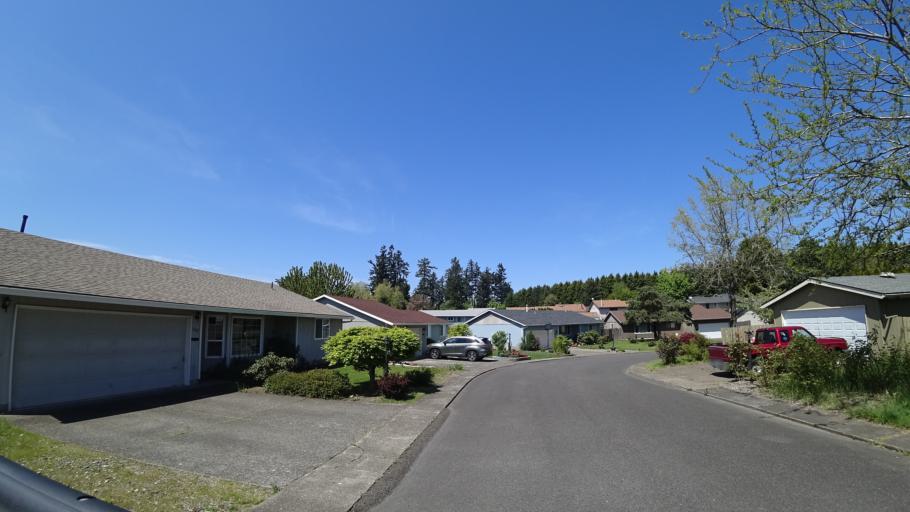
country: US
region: Oregon
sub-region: Washington County
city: Hillsboro
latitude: 45.5056
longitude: -122.9717
